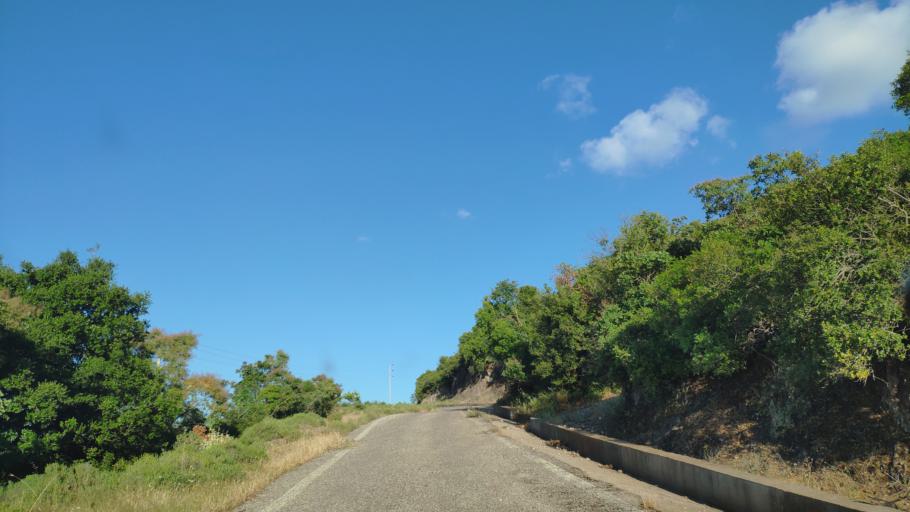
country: GR
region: West Greece
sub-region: Nomos Aitolias kai Akarnanias
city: Fitiai
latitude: 38.6578
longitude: 21.1959
